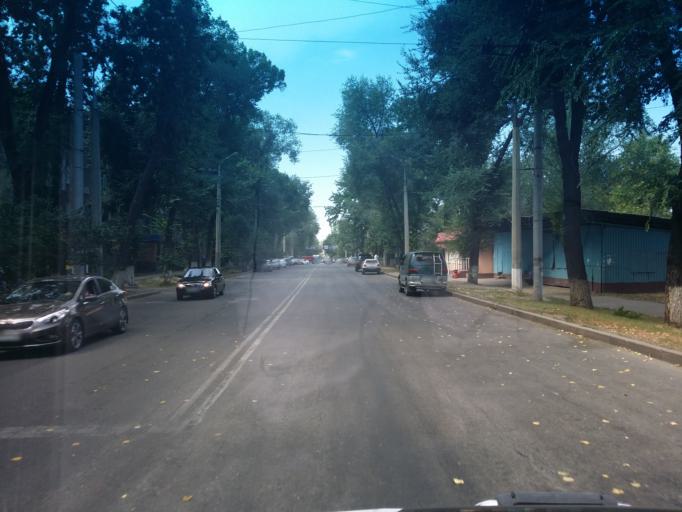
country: KZ
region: Almaty Qalasy
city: Almaty
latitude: 43.2437
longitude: 76.9306
